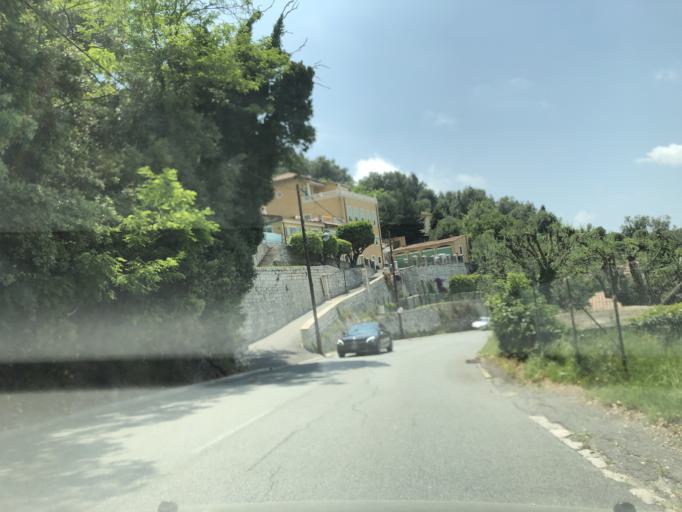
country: FR
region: Provence-Alpes-Cote d'Azur
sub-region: Departement des Alpes-Maritimes
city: Saint-Andre-de-la-Roche
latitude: 43.7246
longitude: 7.2963
